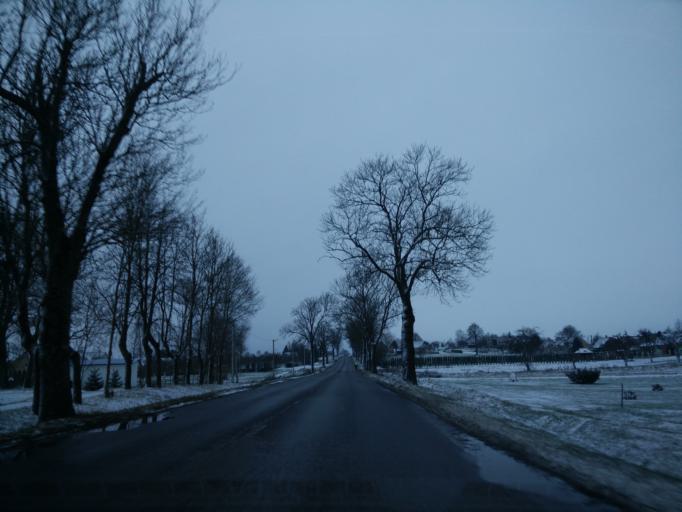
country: LT
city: Kelme
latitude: 55.6213
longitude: 22.9158
